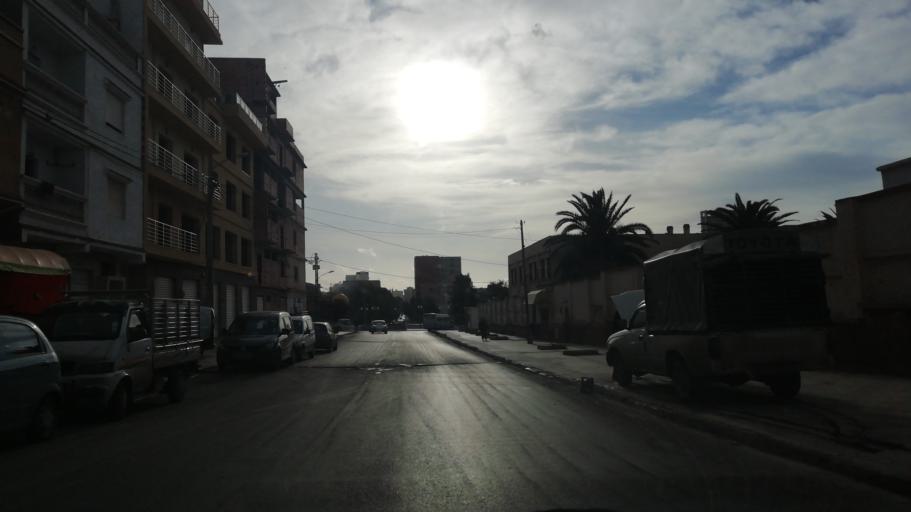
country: DZ
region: Oran
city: Bir el Djir
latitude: 35.7303
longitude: -0.5791
